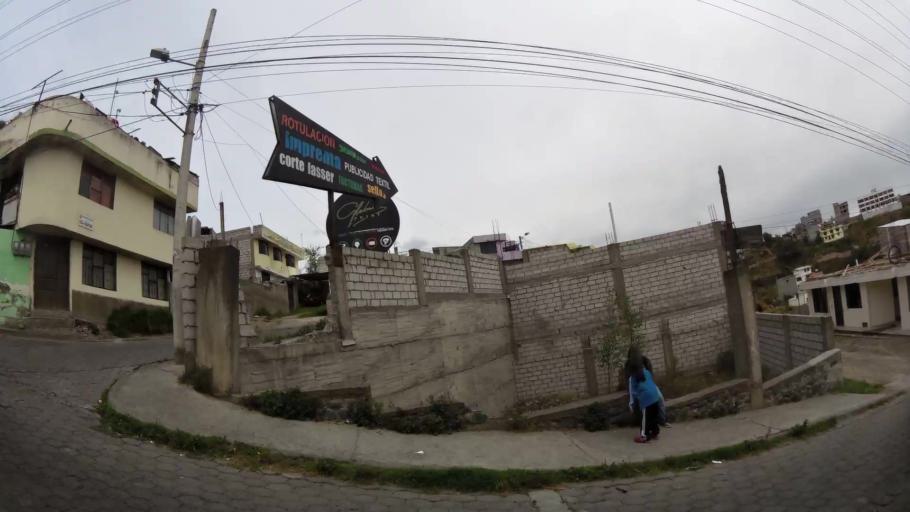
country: EC
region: Cotopaxi
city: Latacunga
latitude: -0.9327
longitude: -78.6104
